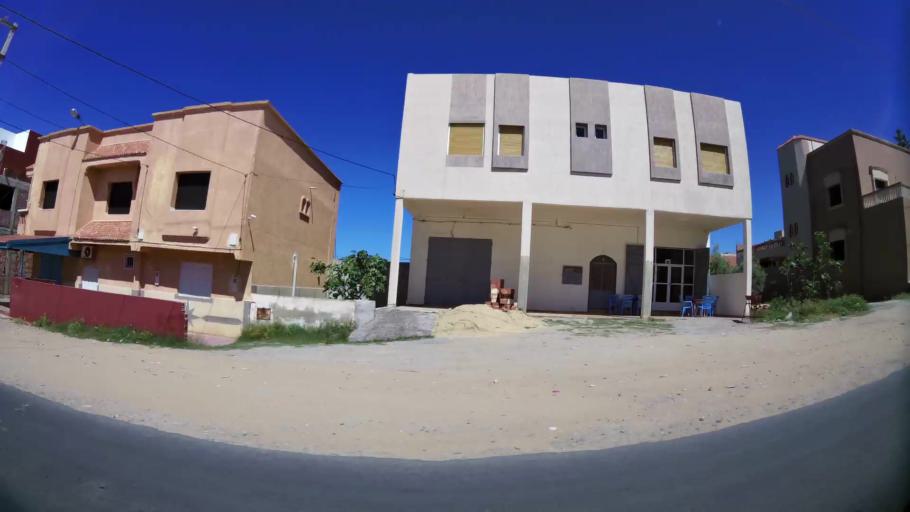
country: MA
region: Oriental
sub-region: Berkane-Taourirt
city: Madagh
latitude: 35.1304
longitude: -2.4246
